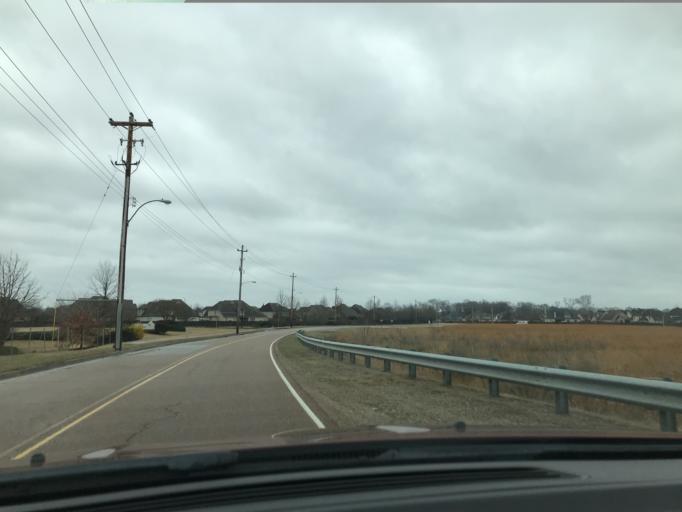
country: US
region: Tennessee
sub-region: Shelby County
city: Collierville
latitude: 35.0902
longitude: -89.7091
